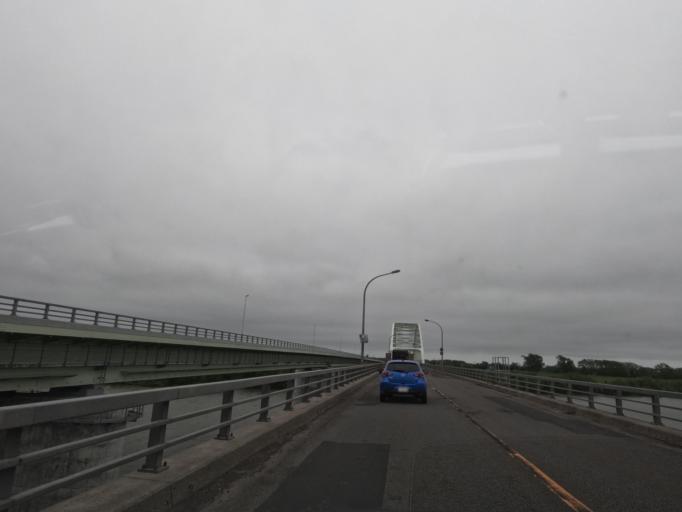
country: JP
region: Hokkaido
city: Ebetsu
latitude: 43.1349
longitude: 141.5108
